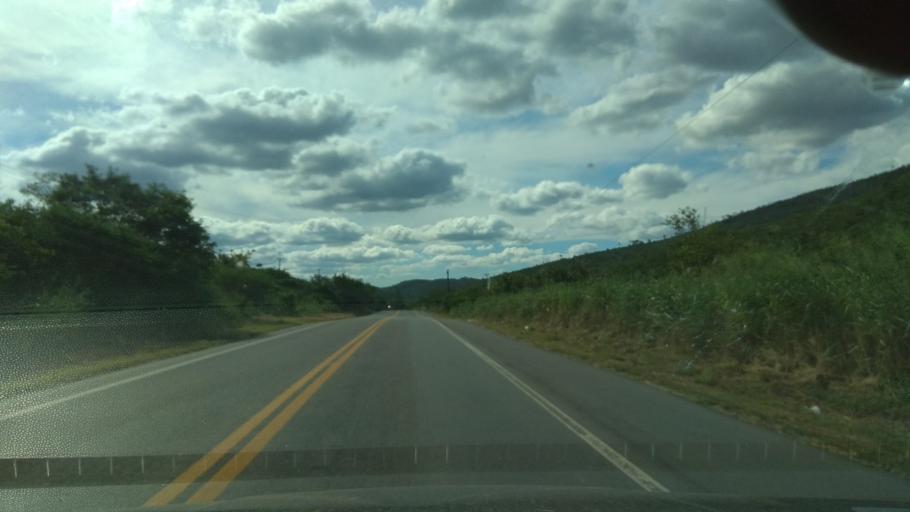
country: BR
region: Bahia
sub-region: Jequie
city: Jequie
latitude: -13.9094
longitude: -40.0168
